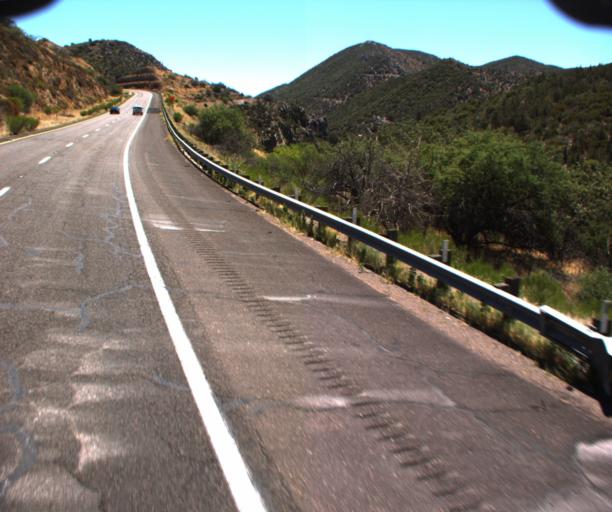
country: US
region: Arizona
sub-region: Gila County
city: Tonto Basin
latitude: 33.9604
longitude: -111.3978
